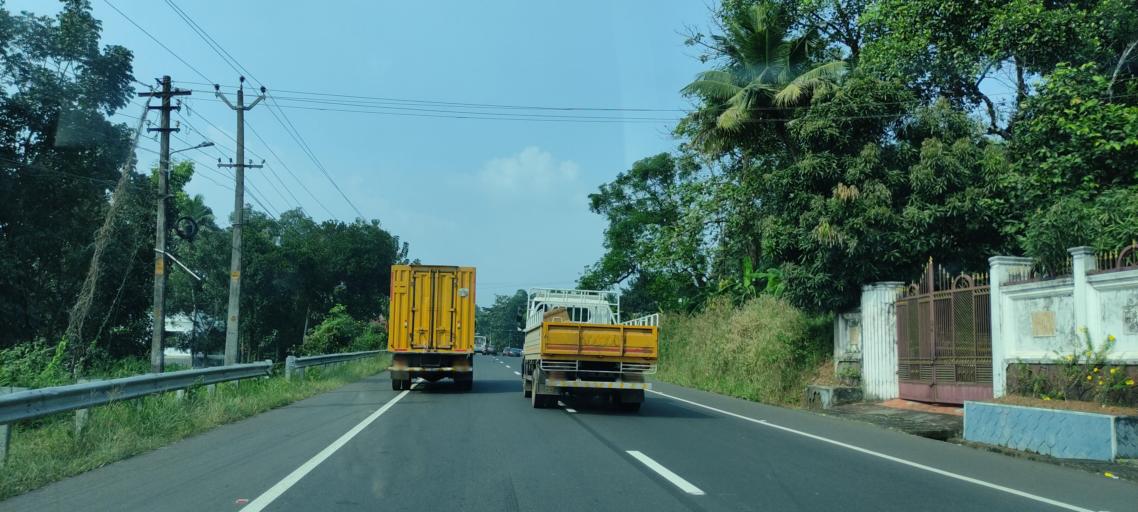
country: IN
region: Kerala
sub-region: Alappuzha
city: Chengannur
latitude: 9.2637
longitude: 76.6563
